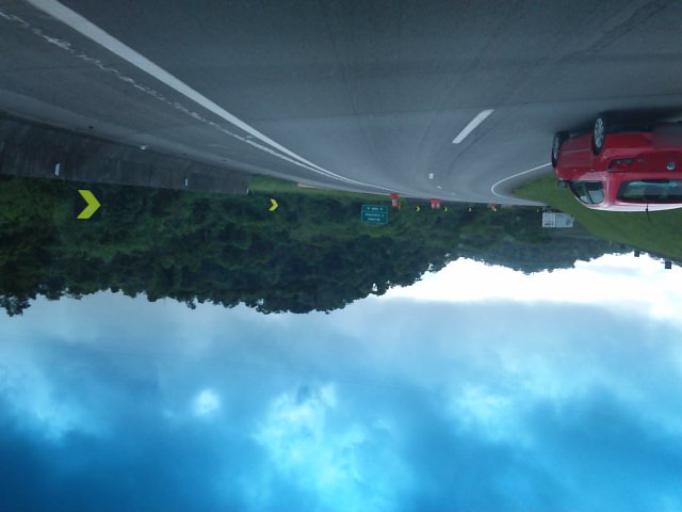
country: BR
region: Parana
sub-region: Antonina
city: Antonina
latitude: -25.0974
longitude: -48.6726
